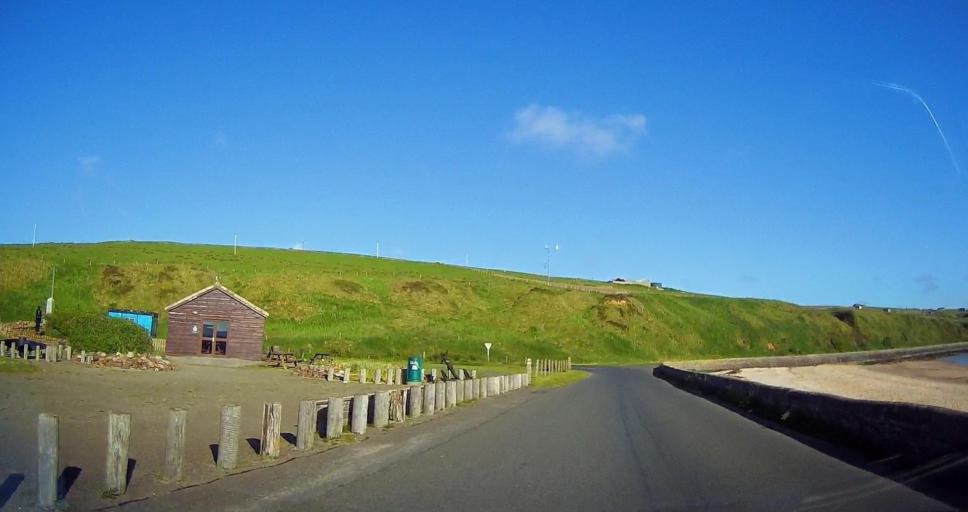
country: GB
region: Scotland
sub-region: Orkney Islands
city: Orkney
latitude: 58.9608
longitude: -2.9702
